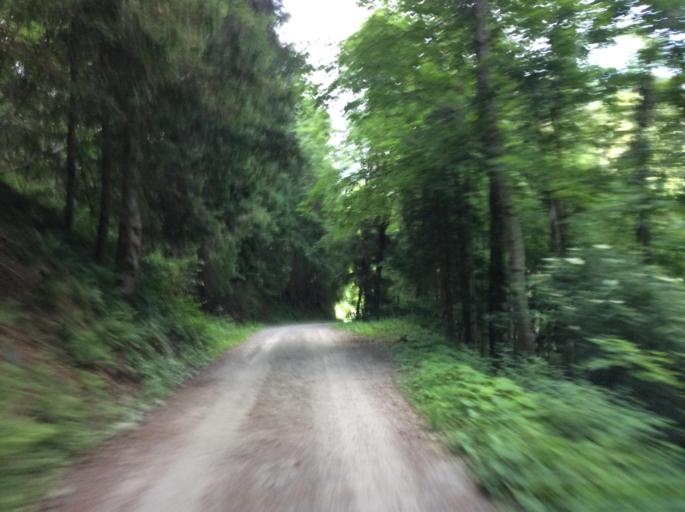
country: AT
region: Salzburg
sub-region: Politischer Bezirk Sankt Johann im Pongau
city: Forstau
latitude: 47.4086
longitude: 13.5711
